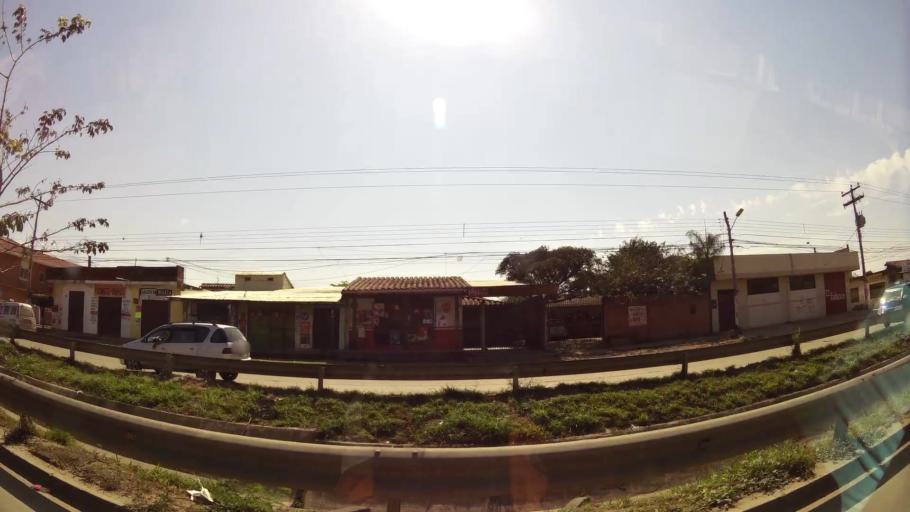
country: BO
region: Santa Cruz
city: Santa Cruz de la Sierra
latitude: -17.7491
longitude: -63.1255
